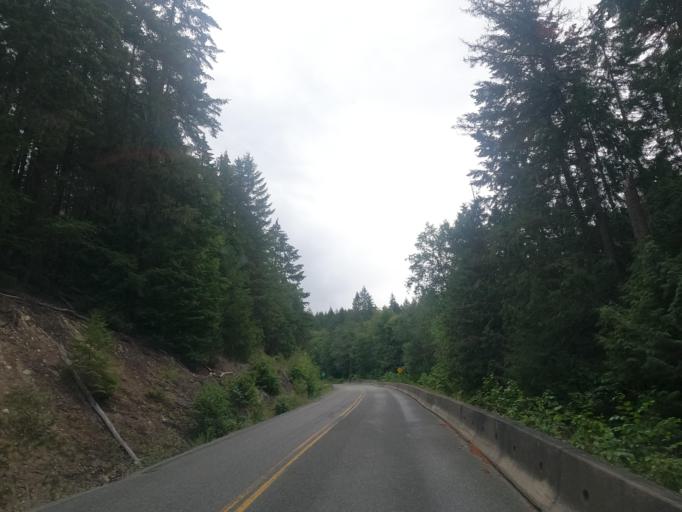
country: CA
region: British Columbia
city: Pemberton
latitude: 50.3019
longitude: -122.5808
